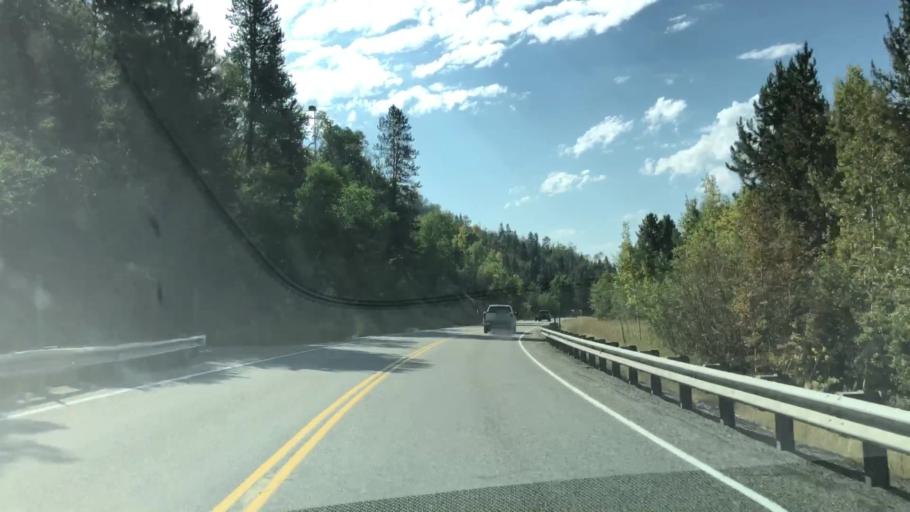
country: US
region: Idaho
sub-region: Teton County
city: Victor
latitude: 43.2773
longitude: -111.1147
